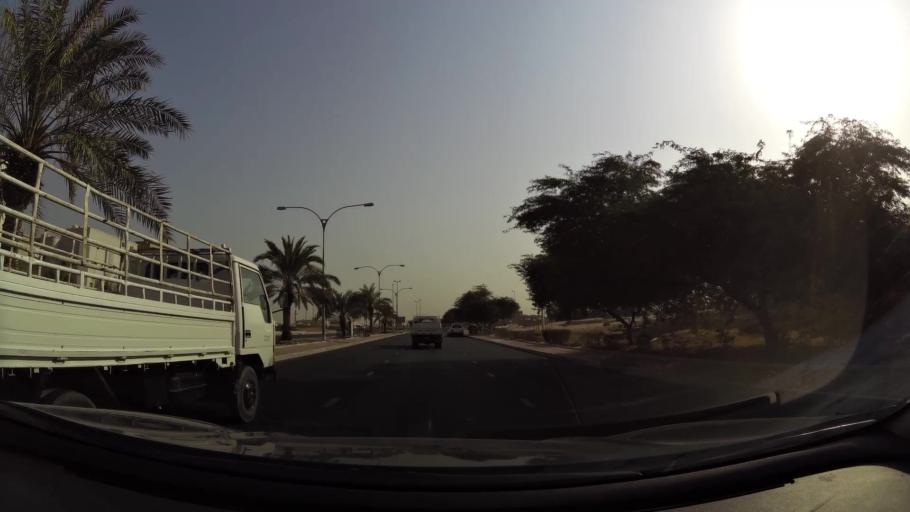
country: KW
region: Al Ahmadi
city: Ar Riqqah
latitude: 29.1231
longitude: 48.1047
